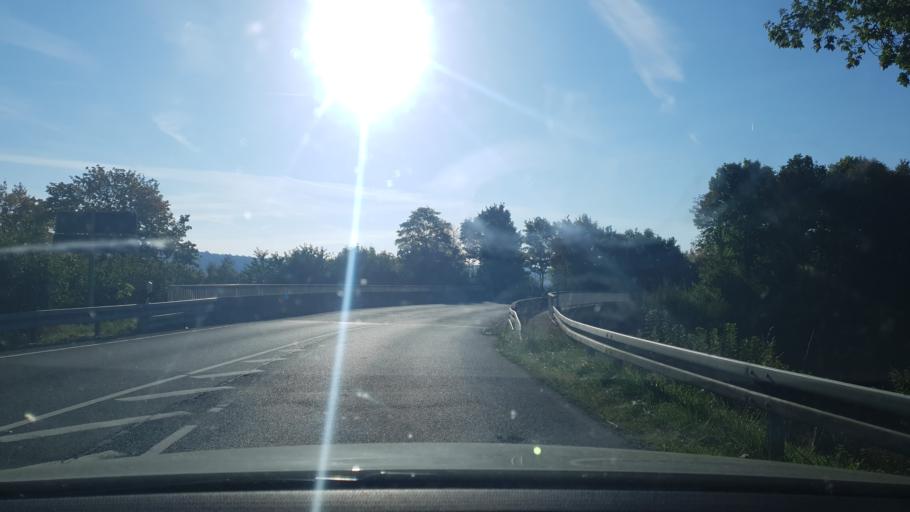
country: DE
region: Hesse
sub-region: Regierungsbezirk Giessen
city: Langgons
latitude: 50.4783
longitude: 8.6549
